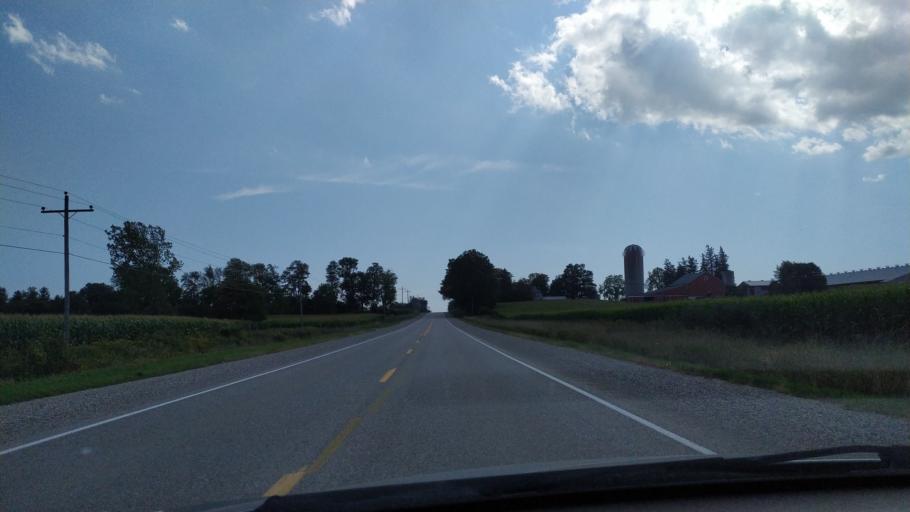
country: CA
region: Ontario
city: Ingersoll
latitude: 43.1304
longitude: -80.8886
